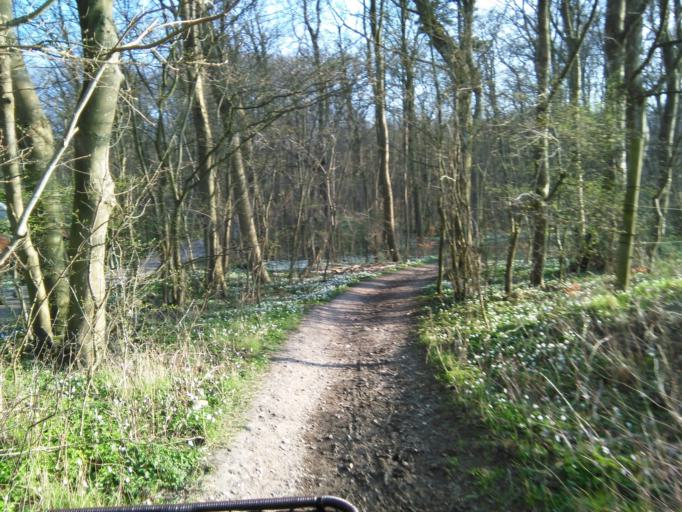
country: DK
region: Central Jutland
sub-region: Arhus Kommune
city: Beder
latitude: 56.0902
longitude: 10.1966
